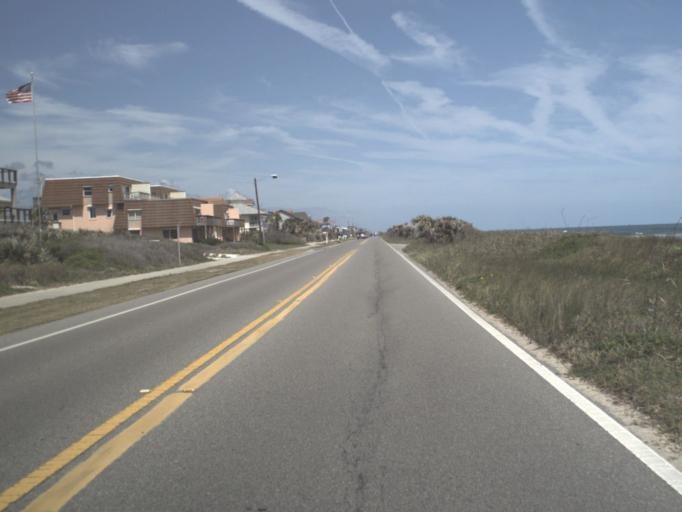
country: US
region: Florida
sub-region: Flagler County
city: Flagler Beach
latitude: 29.4443
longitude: -81.1103
